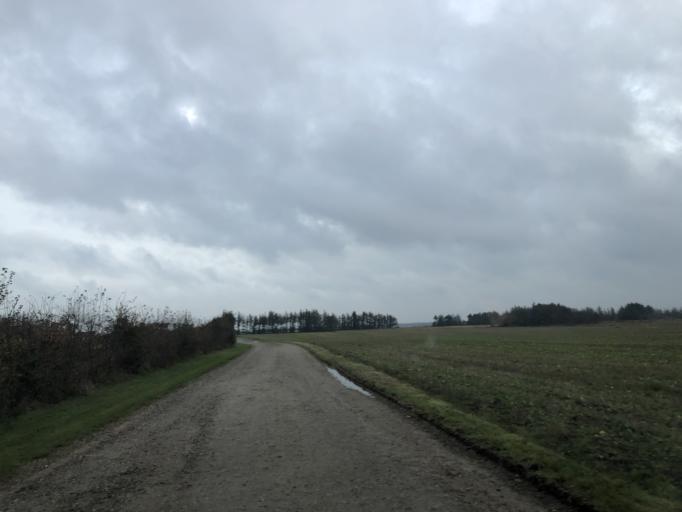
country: DK
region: Central Jutland
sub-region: Holstebro Kommune
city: Ulfborg
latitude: 56.3176
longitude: 8.2216
